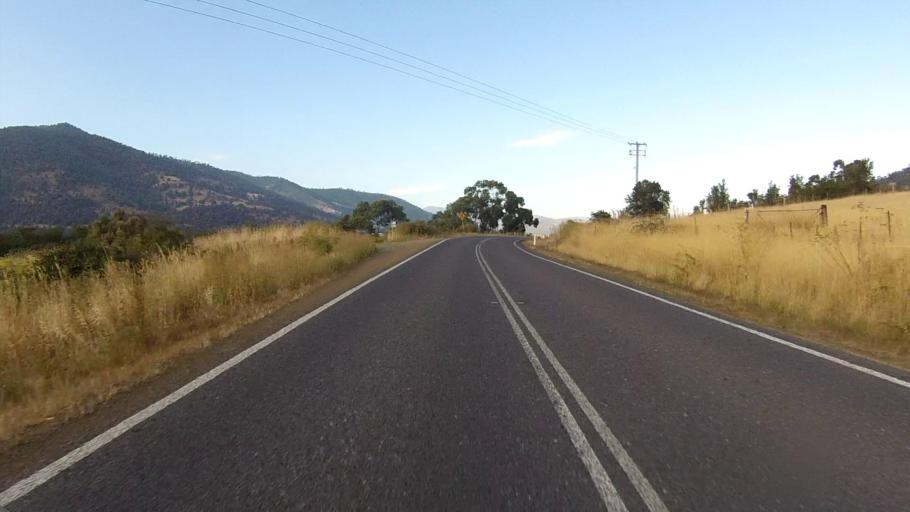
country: AU
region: Tasmania
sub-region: Glenorchy
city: Granton
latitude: -42.7499
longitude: 147.1525
